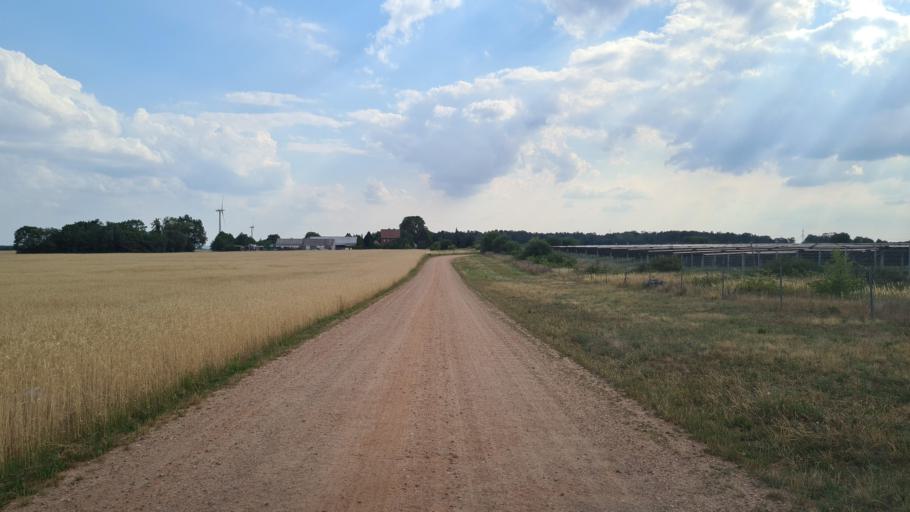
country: DE
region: Saxony-Anhalt
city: Abtsdorf
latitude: 51.9125
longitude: 12.6974
